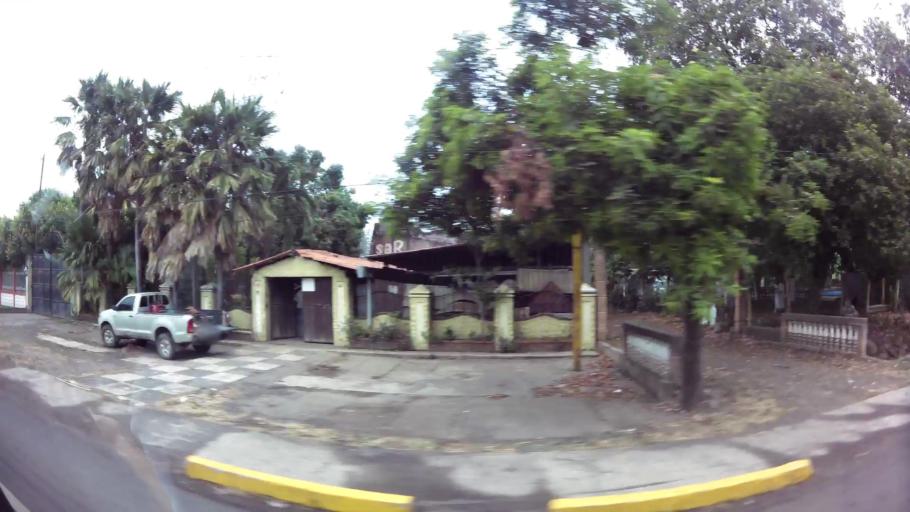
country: NI
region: Chinandega
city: Chinandega
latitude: 12.6199
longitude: -87.1139
